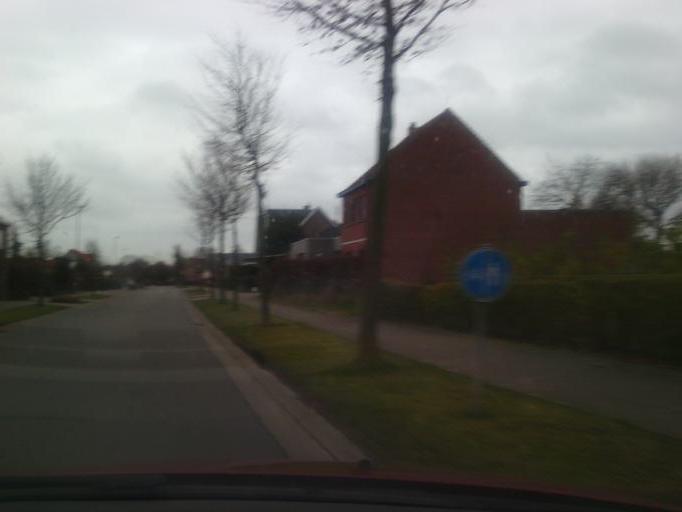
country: BE
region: Flanders
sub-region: Provincie Oost-Vlaanderen
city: Berlare
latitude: 51.0616
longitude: 4.0039
